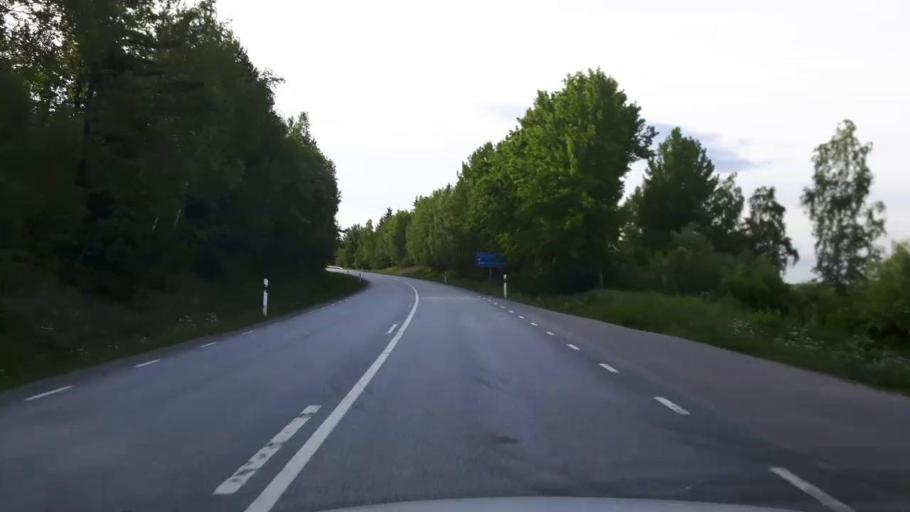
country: SE
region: Uppsala
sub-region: Habo Kommun
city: Balsta
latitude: 59.6500
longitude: 17.5624
